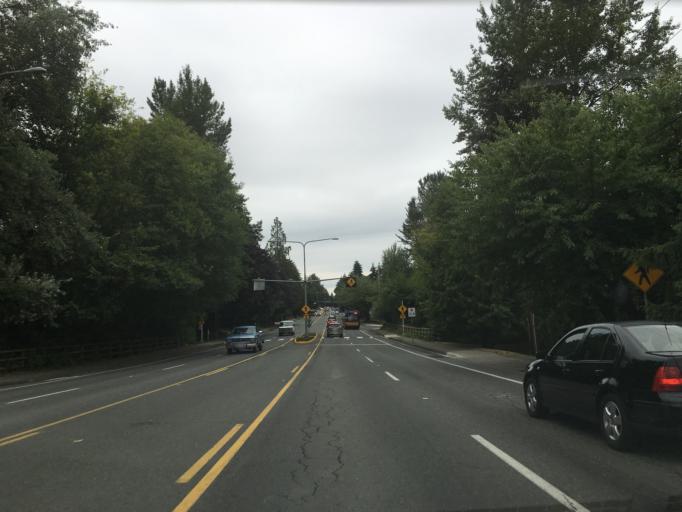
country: US
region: Washington
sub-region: King County
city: Inglewood-Finn Hill
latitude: 47.7163
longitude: -122.2078
